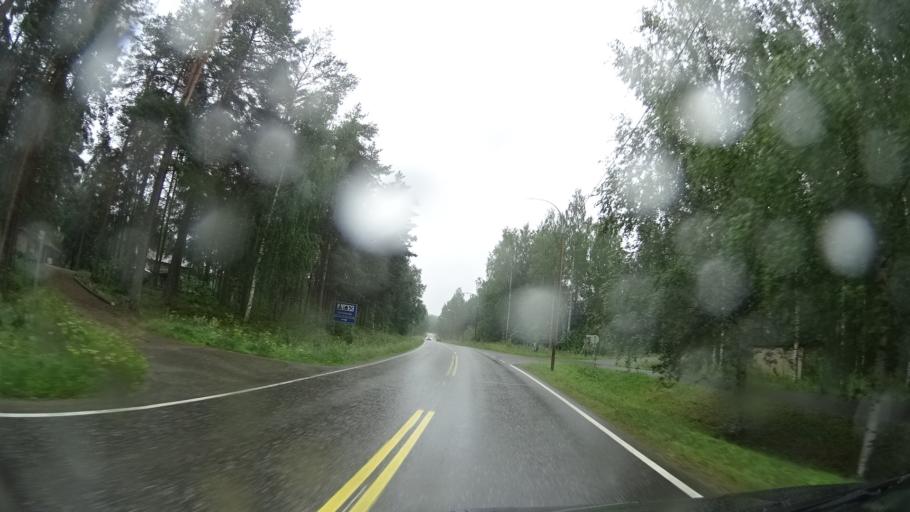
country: FI
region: North Karelia
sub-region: Keski-Karjala
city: Raeaekkylae
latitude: 62.3124
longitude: 29.5924
